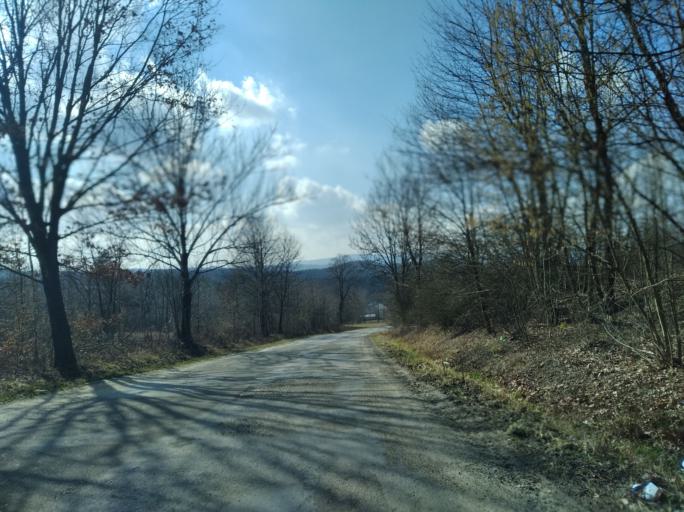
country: PL
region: Subcarpathian Voivodeship
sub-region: Powiat debicki
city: Brzostek
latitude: 49.8900
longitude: 21.4804
